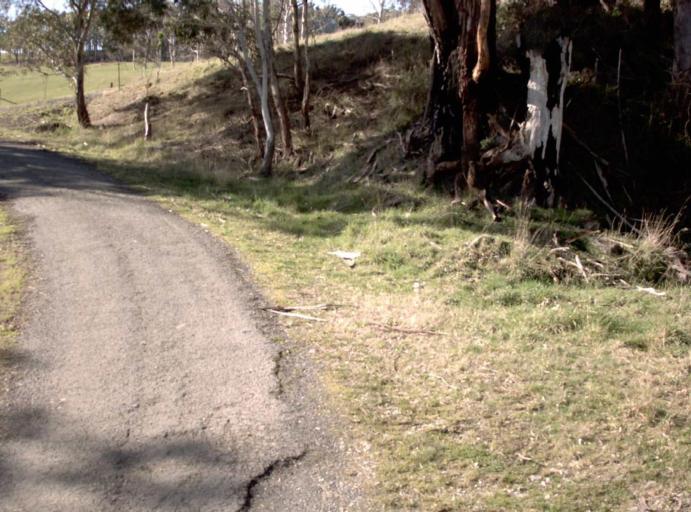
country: AU
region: Tasmania
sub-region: Launceston
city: Mayfield
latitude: -41.2538
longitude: 147.1561
